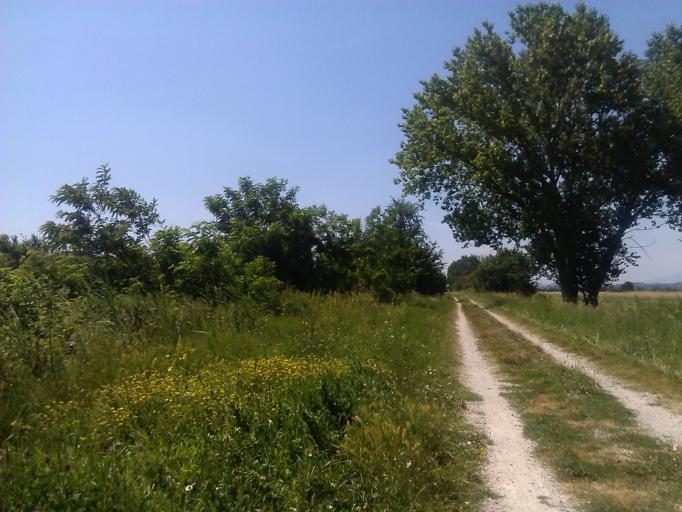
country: IT
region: Tuscany
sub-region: Province of Arezzo
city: Cesa
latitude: 43.3497
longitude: 11.8265
